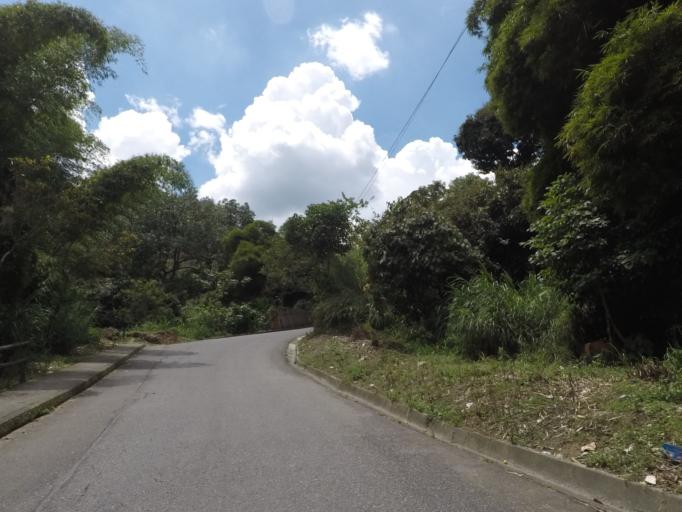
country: CO
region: Antioquia
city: Medellin
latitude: 6.2650
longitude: -75.6286
